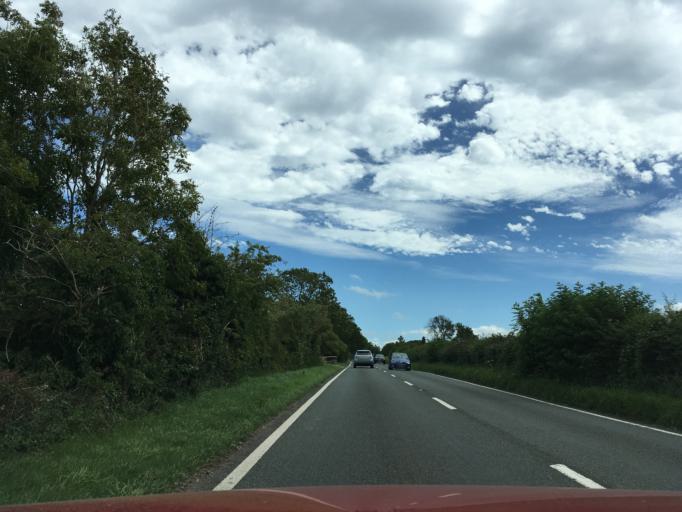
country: GB
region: England
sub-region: Somerset
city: Wells
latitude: 51.2217
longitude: -2.6942
